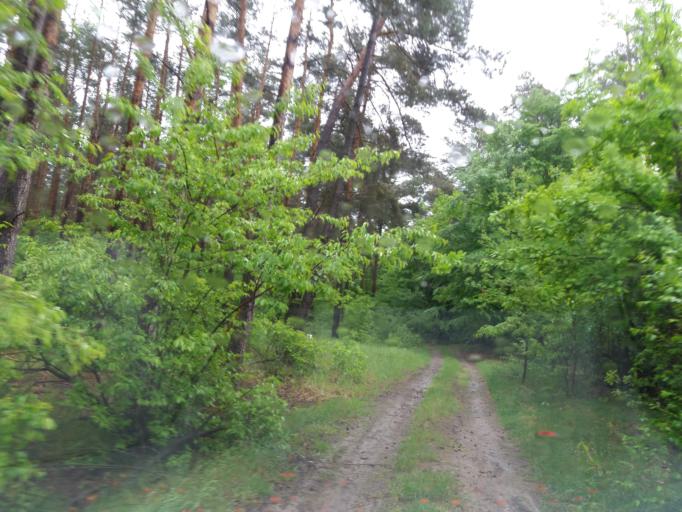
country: PL
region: Lubusz
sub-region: Powiat strzelecko-drezdenecki
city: Dobiegniew
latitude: 53.0130
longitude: 15.8438
